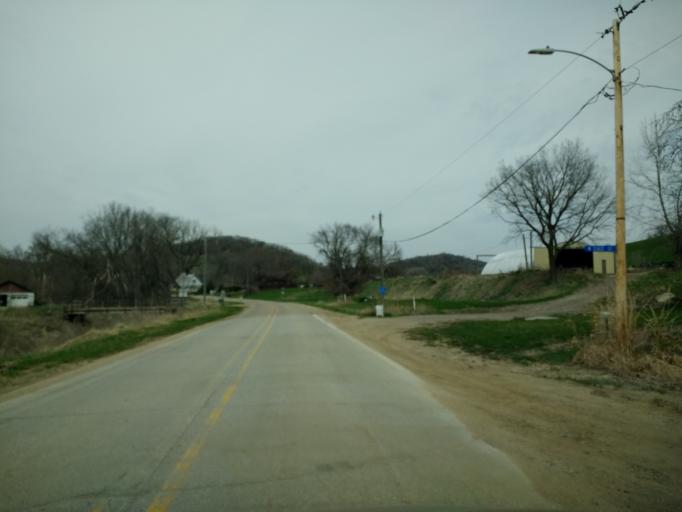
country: US
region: Iowa
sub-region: Monona County
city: Mapleton
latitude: 42.2302
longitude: -95.9369
